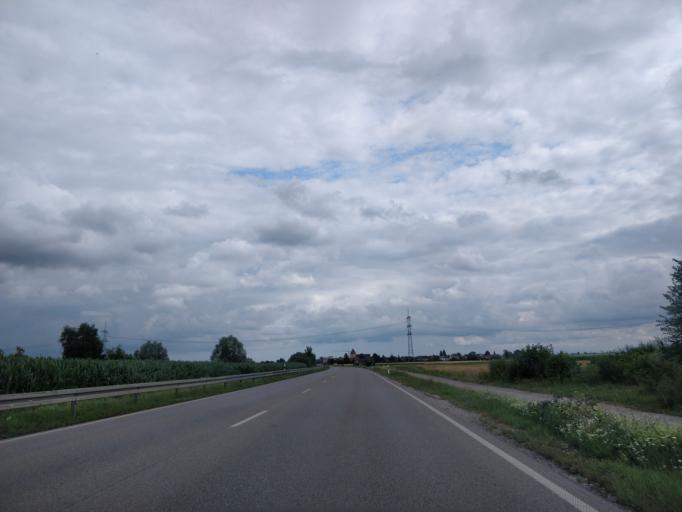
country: DE
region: Bavaria
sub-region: Swabia
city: Kissing
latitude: 48.2902
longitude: 10.9665
